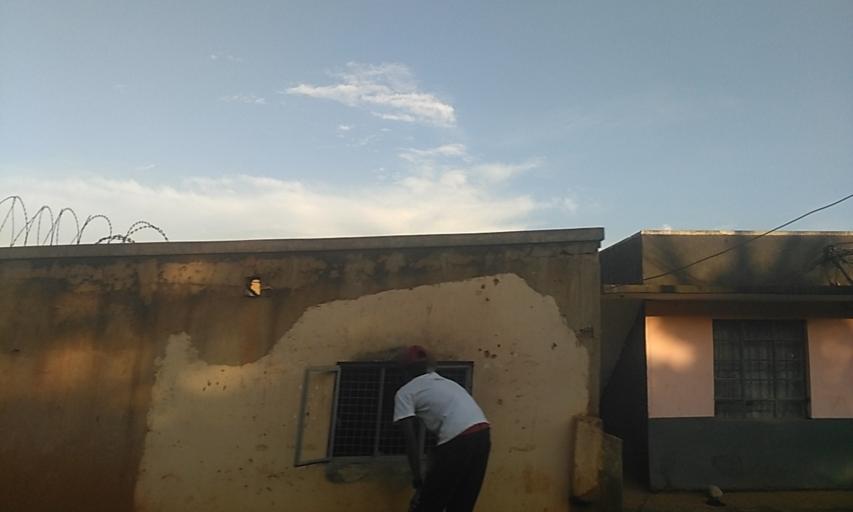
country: UG
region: Central Region
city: Kampala Central Division
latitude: 0.3167
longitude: 32.5617
